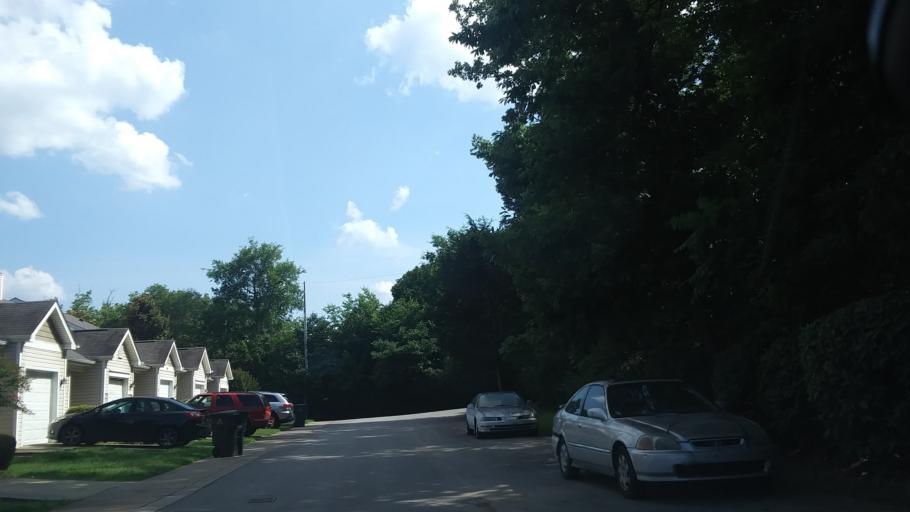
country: US
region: Tennessee
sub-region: Rutherford County
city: La Vergne
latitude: 36.0958
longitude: -86.6336
